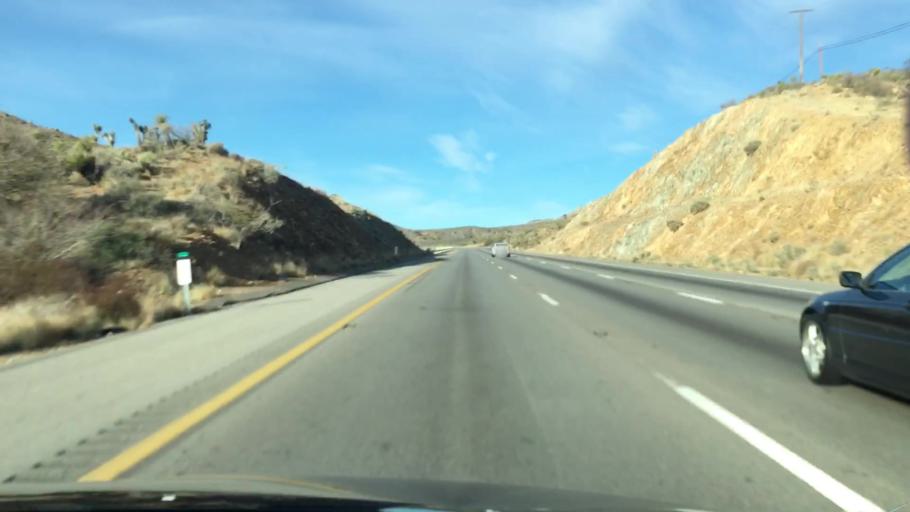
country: US
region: Nevada
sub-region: Clark County
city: Sandy Valley
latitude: 35.4704
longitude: -115.4991
